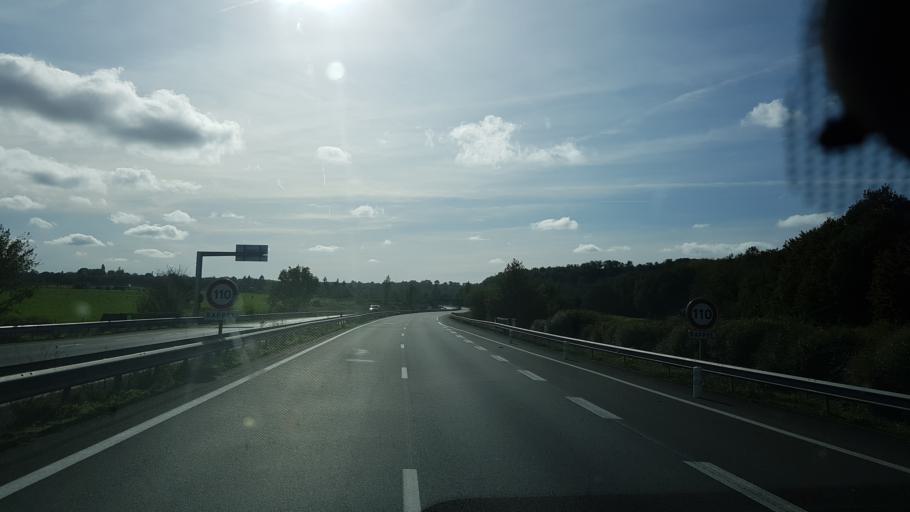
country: FR
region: Poitou-Charentes
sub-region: Departement de la Charente
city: Taponnat-Fleurignac
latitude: 45.7873
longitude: 0.4145
